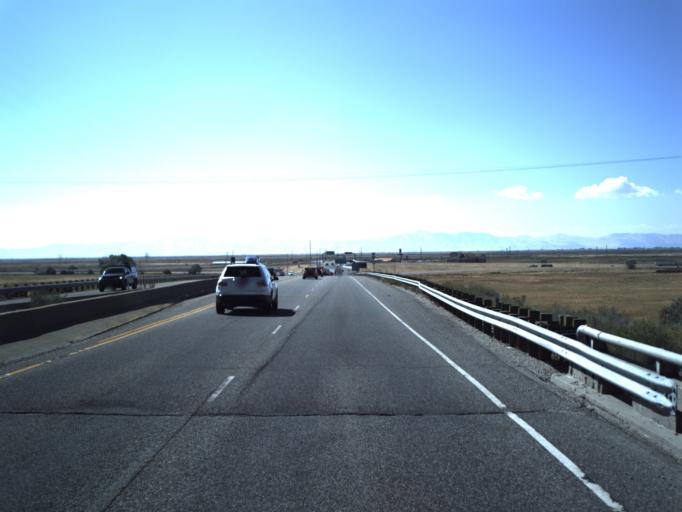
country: US
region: Utah
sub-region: Box Elder County
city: Perry
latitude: 41.4863
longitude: -112.0437
